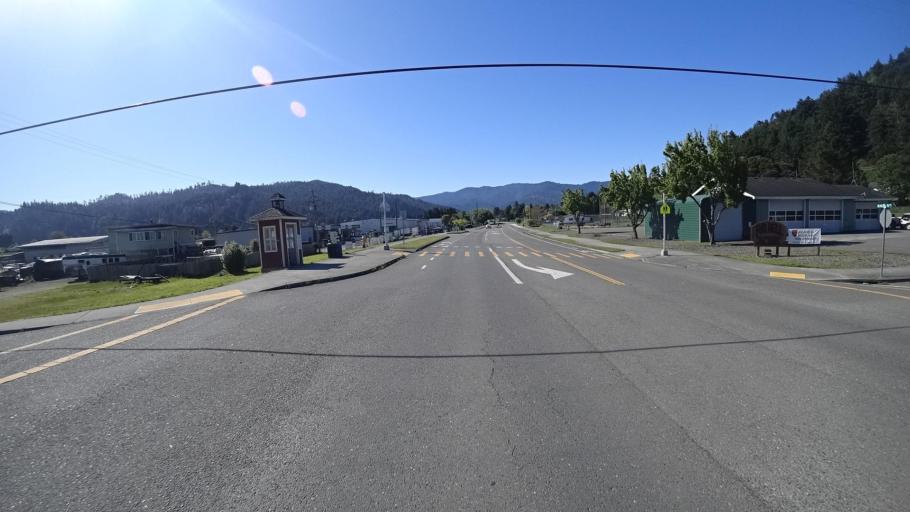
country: US
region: California
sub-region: Humboldt County
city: Rio Dell
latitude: 40.5015
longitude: -124.1066
